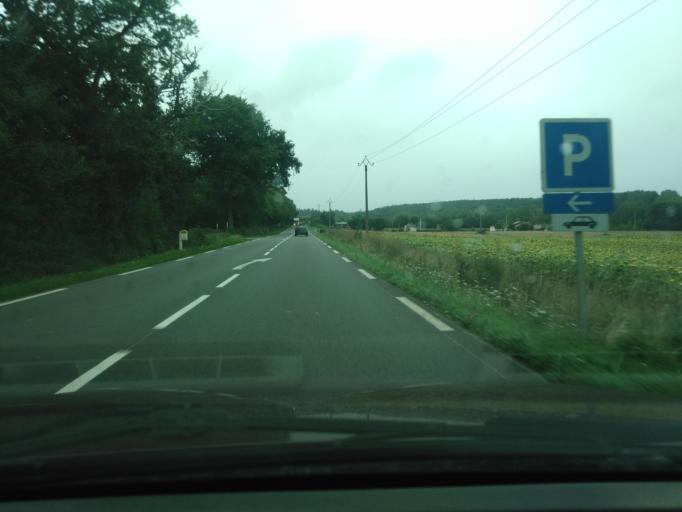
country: FR
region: Pays de la Loire
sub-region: Departement de la Vendee
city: Sainte-Hermine
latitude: 46.5824
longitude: -1.1124
